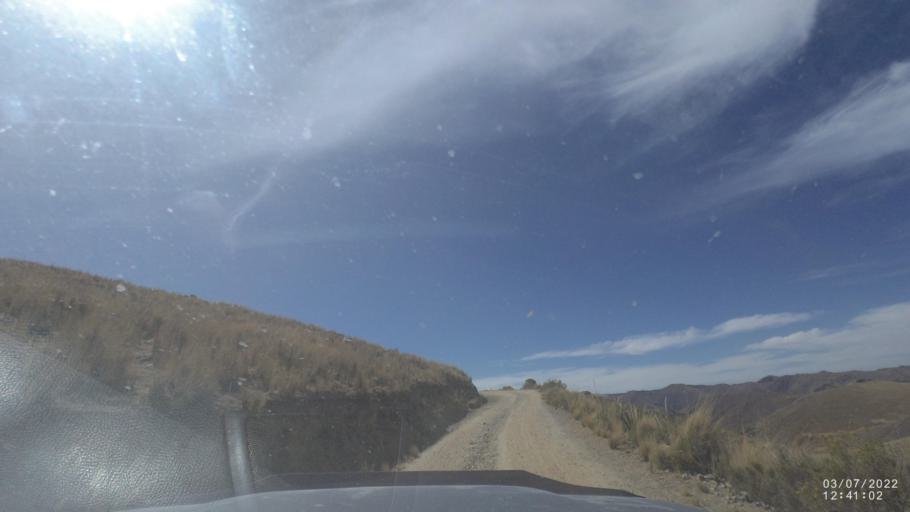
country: BO
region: Cochabamba
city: Irpa Irpa
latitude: -17.7874
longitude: -66.6245
